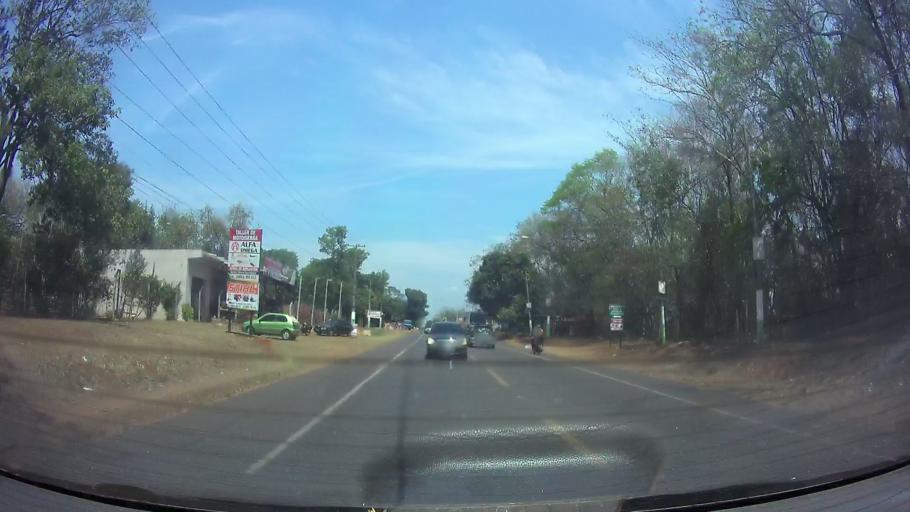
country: PY
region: Central
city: Guarambare
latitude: -25.4316
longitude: -57.4491
